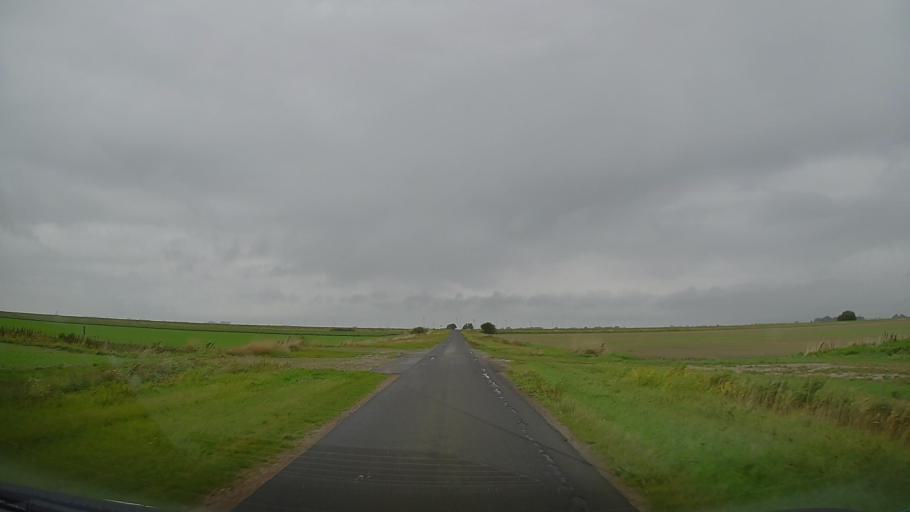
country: DE
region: Schleswig-Holstein
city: Friedrichsgabekoog
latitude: 54.1176
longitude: 8.9781
